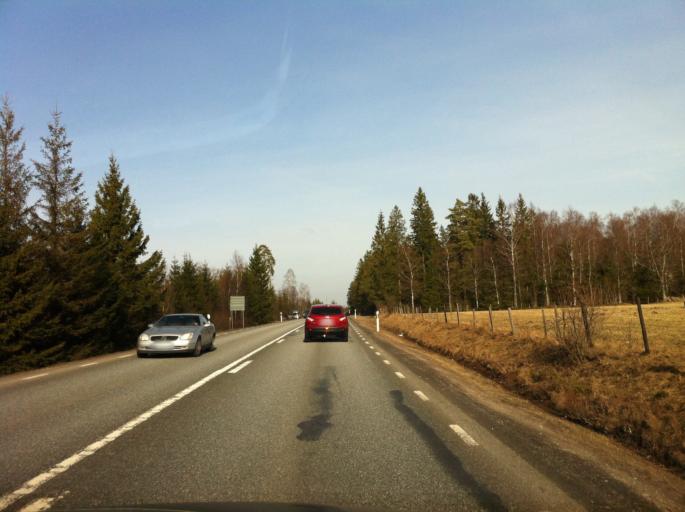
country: SE
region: Joenkoeping
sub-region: Mullsjo Kommun
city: Mullsjoe
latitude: 58.0206
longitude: 13.8280
